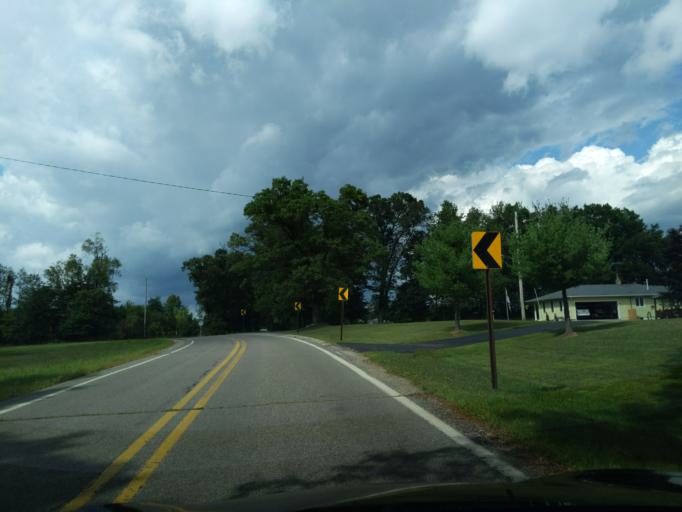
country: US
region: Michigan
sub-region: Jackson County
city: Spring Arbor
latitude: 42.3487
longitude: -84.5563
